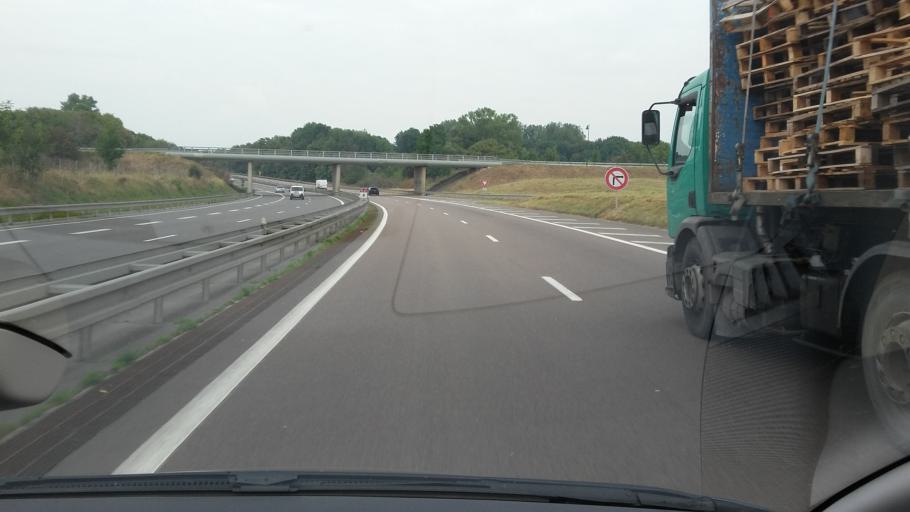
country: FR
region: Champagne-Ardenne
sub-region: Departement de la Marne
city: Warmeriville
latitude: 49.3508
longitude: 4.2027
